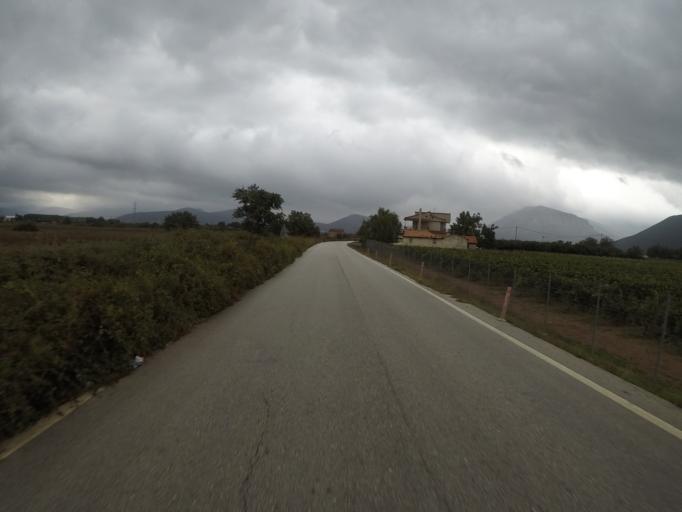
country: GR
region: Peloponnese
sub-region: Nomos Arkadias
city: Tripoli
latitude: 37.5669
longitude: 22.4075
